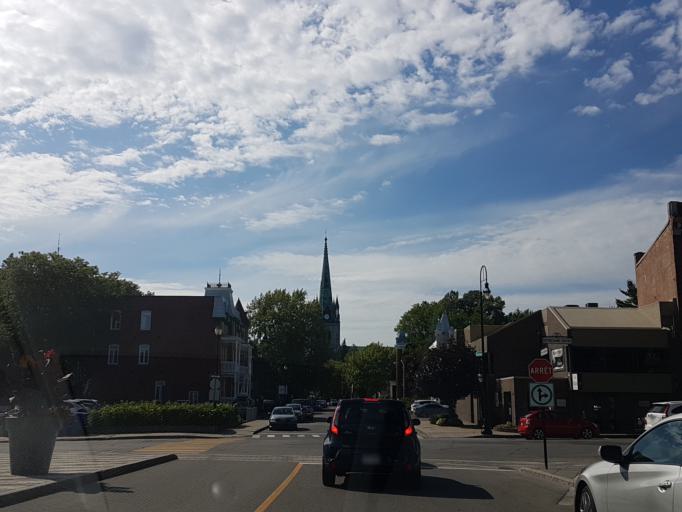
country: CA
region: Quebec
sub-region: Mauricie
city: Trois-Rivieres
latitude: 46.3429
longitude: -72.5394
